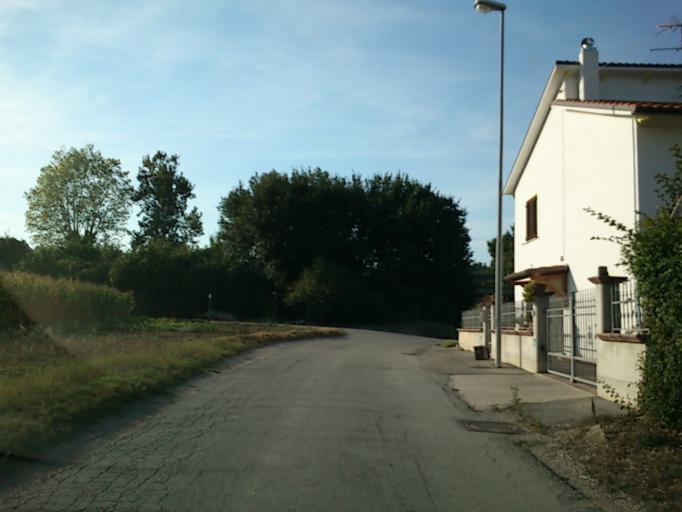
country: IT
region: The Marches
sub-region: Provincia di Pesaro e Urbino
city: Saltara
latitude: 43.7381
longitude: 12.9082
